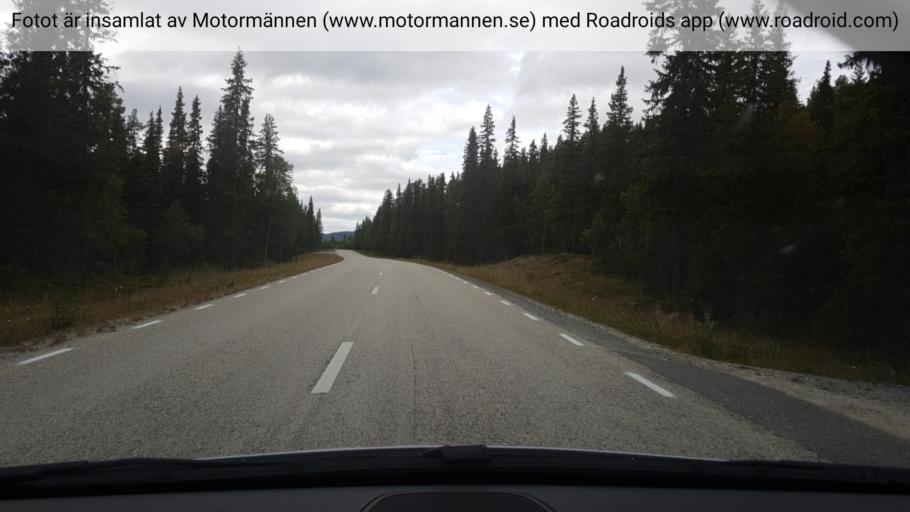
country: SE
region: Jaemtland
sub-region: Are Kommun
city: Are
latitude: 62.8287
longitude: 12.9021
